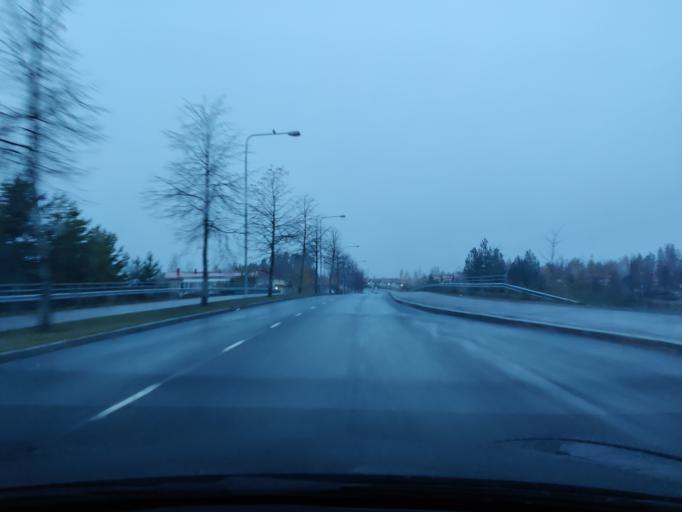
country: FI
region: Northern Savo
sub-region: Kuopio
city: Kuopio
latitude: 62.8258
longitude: 27.6913
